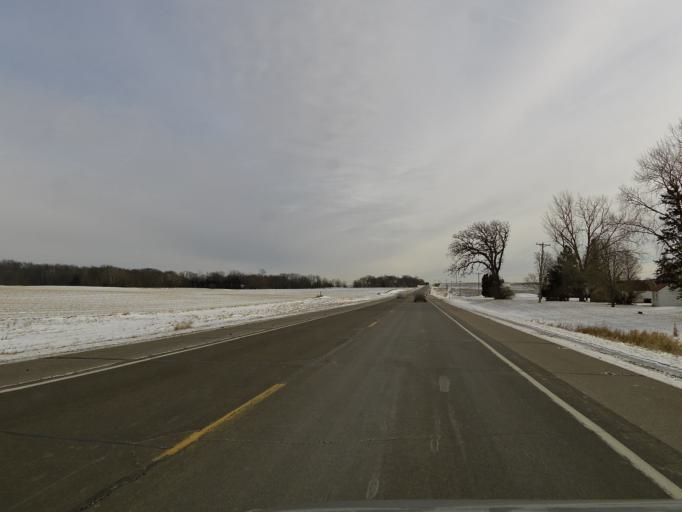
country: US
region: Minnesota
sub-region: Scott County
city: Jordan
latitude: 44.6742
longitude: -93.5891
